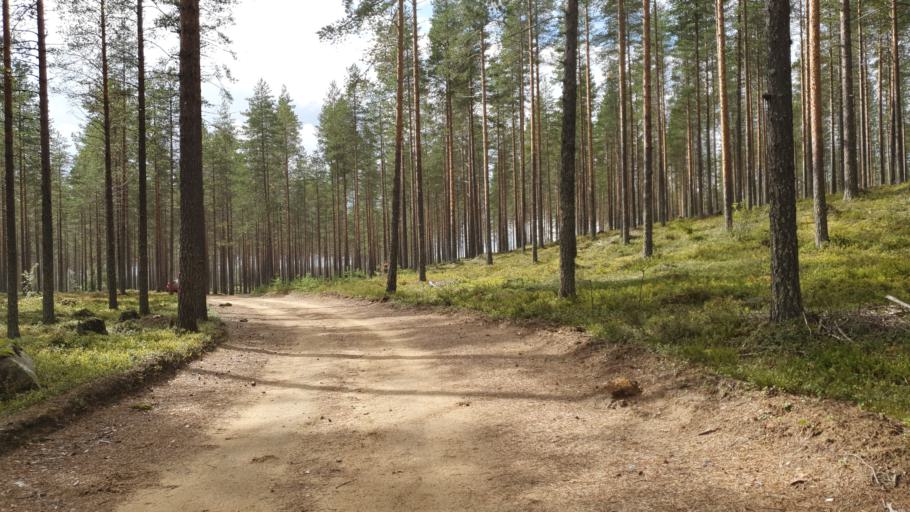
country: FI
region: Kainuu
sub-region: Kehys-Kainuu
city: Kuhmo
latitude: 64.1495
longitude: 29.3854
